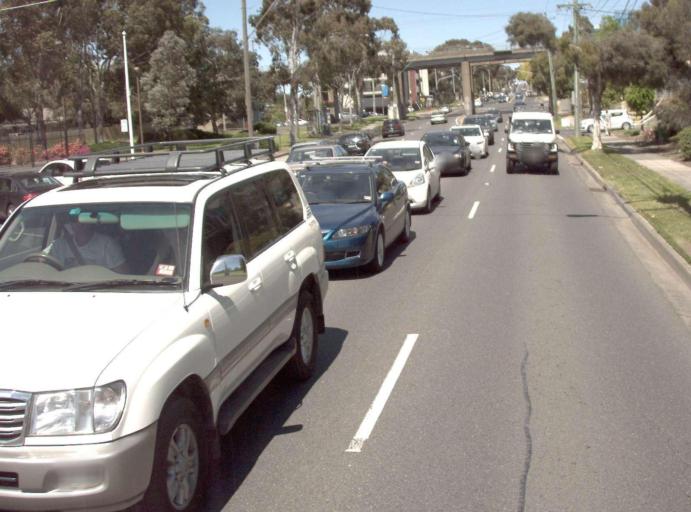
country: AU
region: Victoria
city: Burwood East
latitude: -37.8749
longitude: 145.1479
